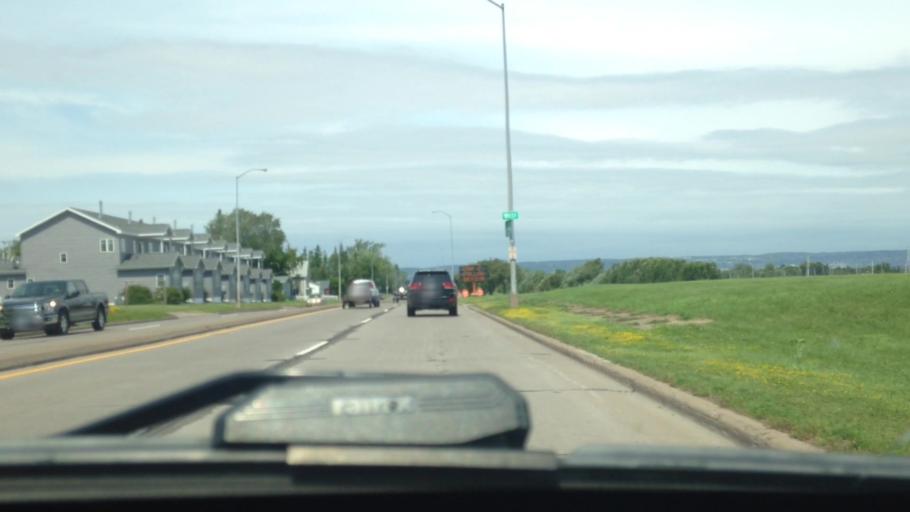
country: US
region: Wisconsin
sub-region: Douglas County
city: Superior
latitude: 46.7118
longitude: -92.0539
